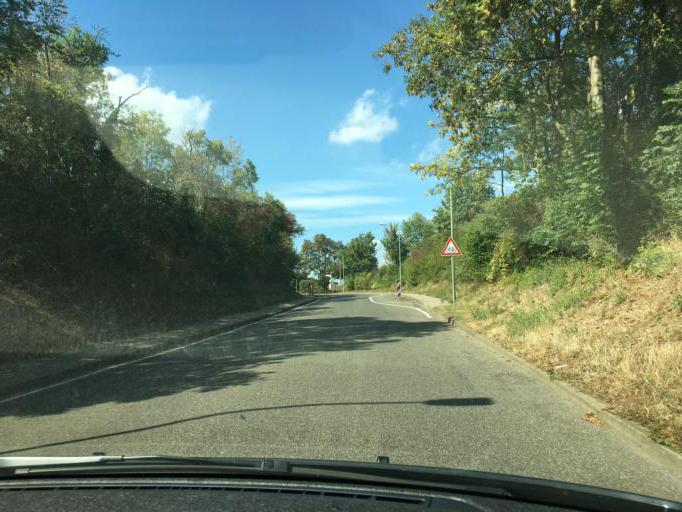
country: DE
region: North Rhine-Westphalia
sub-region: Regierungsbezirk Koln
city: Nideggen
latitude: 50.6806
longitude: 6.5181
